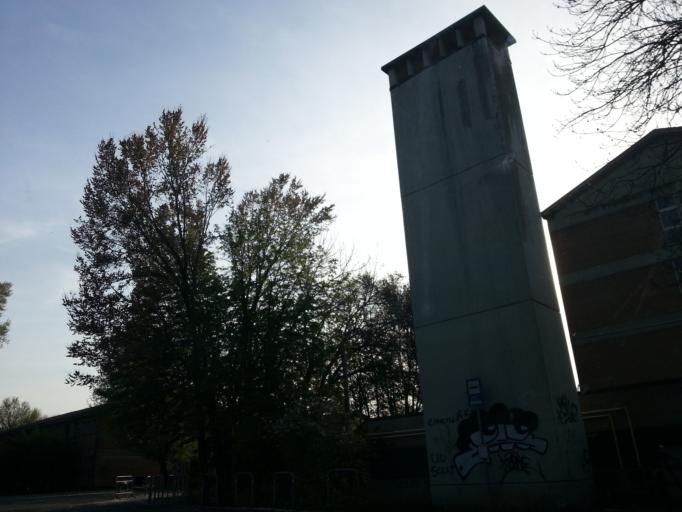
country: IT
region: Emilia-Romagna
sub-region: Provincia di Reggio Emilia
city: Forche
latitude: 44.6641
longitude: 10.5899
